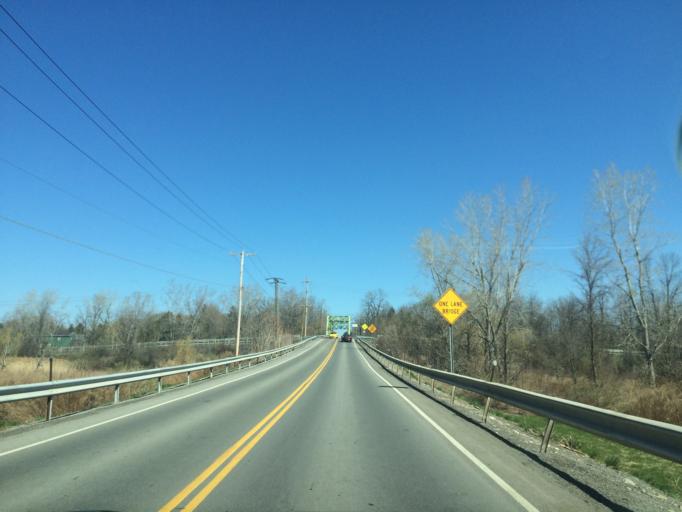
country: US
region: New York
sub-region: Wayne County
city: Palmyra
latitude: 43.0622
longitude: -77.2575
